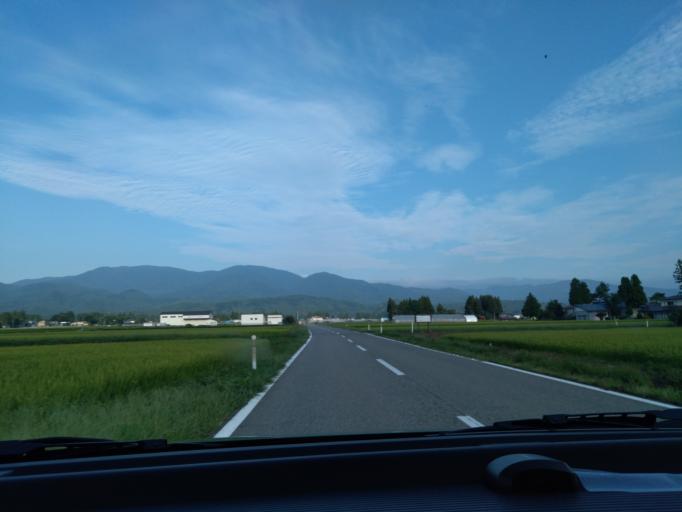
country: JP
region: Akita
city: Kakunodatemachi
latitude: 39.5740
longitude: 140.5863
